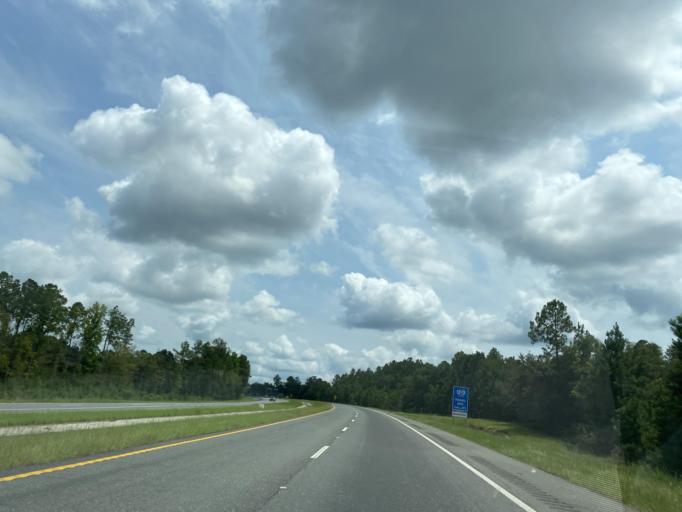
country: US
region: Georgia
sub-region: Ware County
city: Deenwood
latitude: 31.2962
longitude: -82.4520
